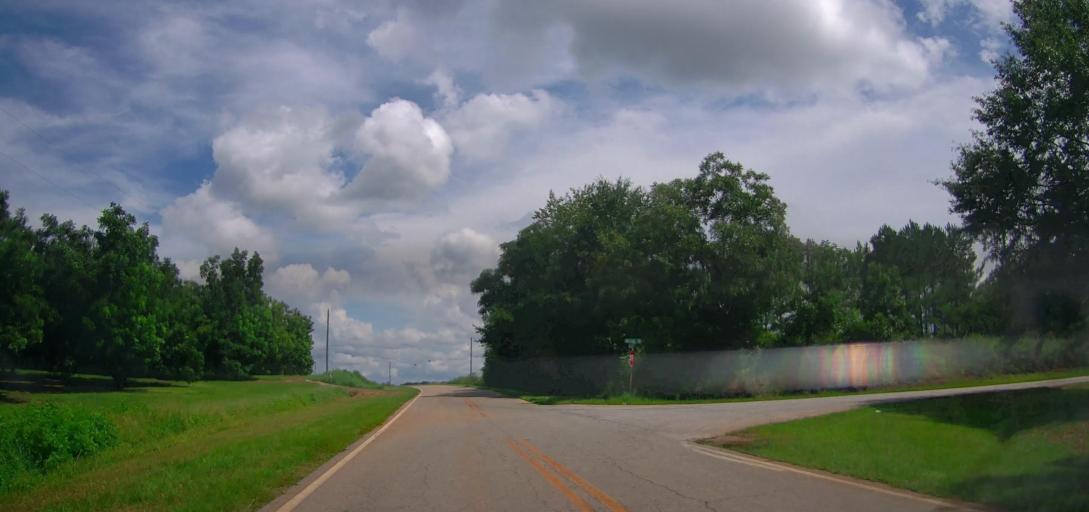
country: US
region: Georgia
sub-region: Houston County
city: Perry
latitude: 32.5212
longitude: -83.7726
